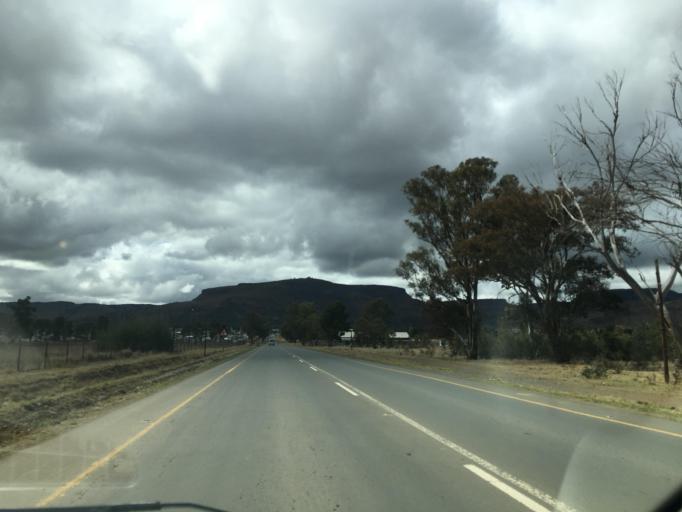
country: ZA
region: Eastern Cape
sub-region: Chris Hani District Municipality
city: Cala
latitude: -31.5305
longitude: 27.6765
